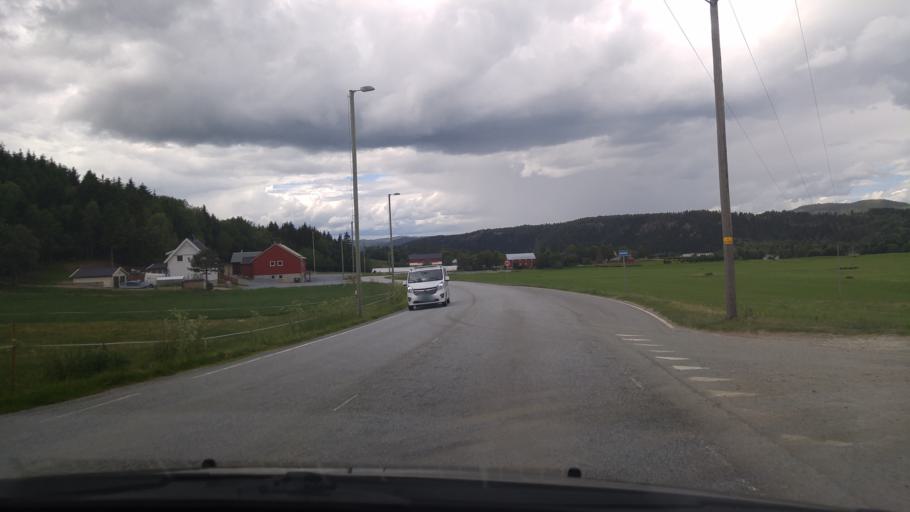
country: NO
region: Nord-Trondelag
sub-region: Steinkjer
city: Steinkjer
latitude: 64.0967
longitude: 11.4469
